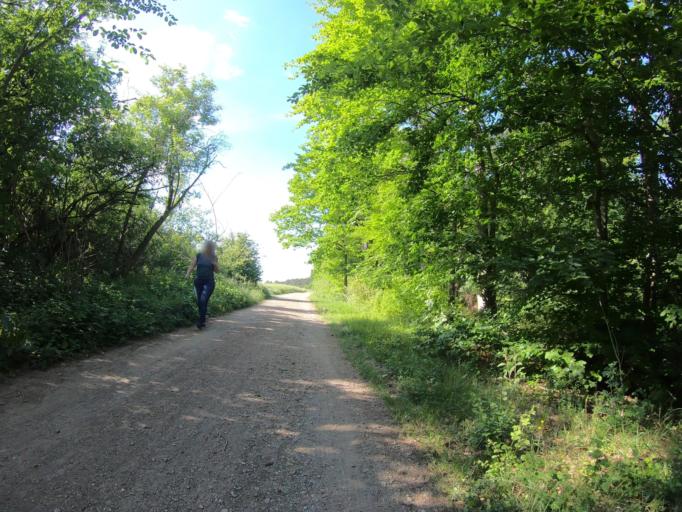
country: DE
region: Lower Saxony
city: Wolfenbuettel
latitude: 52.1858
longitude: 10.5289
